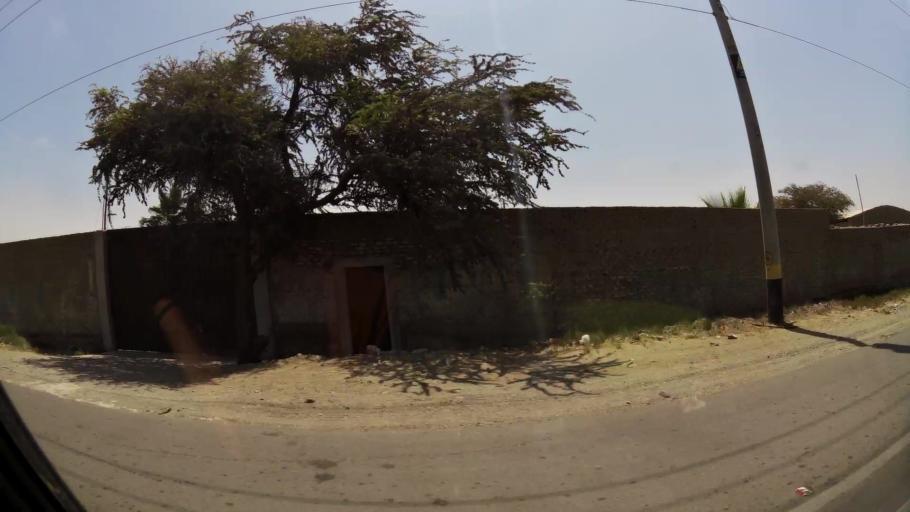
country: PE
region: La Libertad
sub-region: Provincia de Pacasmayo
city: San Pedro de Lloc
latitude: -7.4184
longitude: -79.5053
